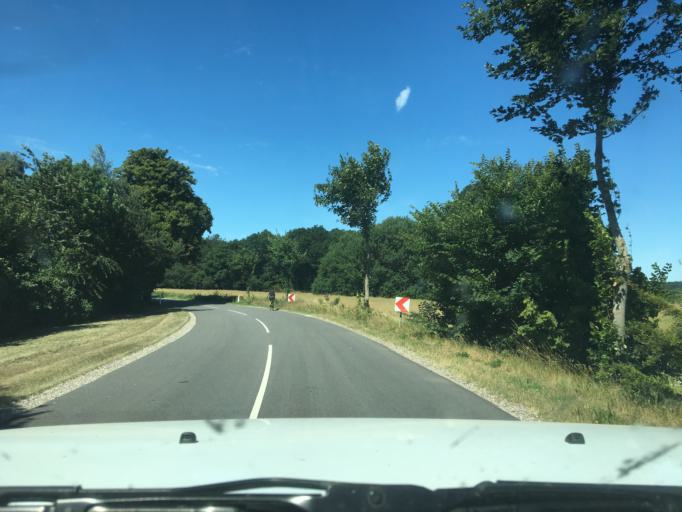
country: DK
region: Central Jutland
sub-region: Syddjurs Kommune
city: Hornslet
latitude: 56.3265
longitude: 10.3605
